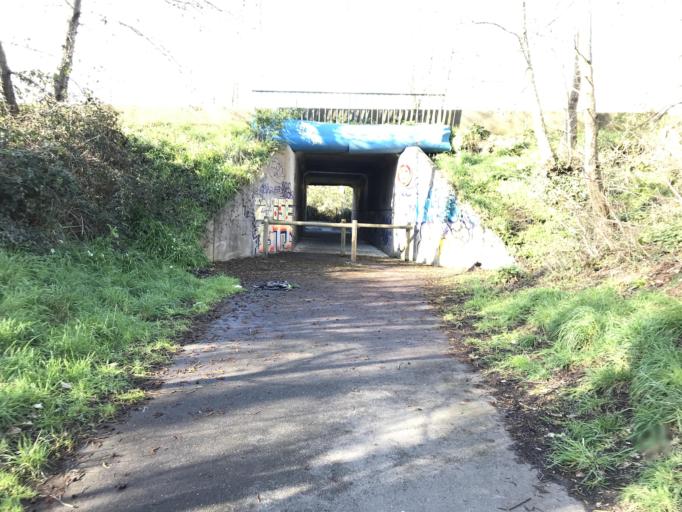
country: FR
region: Brittany
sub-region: Departement du Finistere
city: Brest
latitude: 48.3935
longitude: -4.4425
